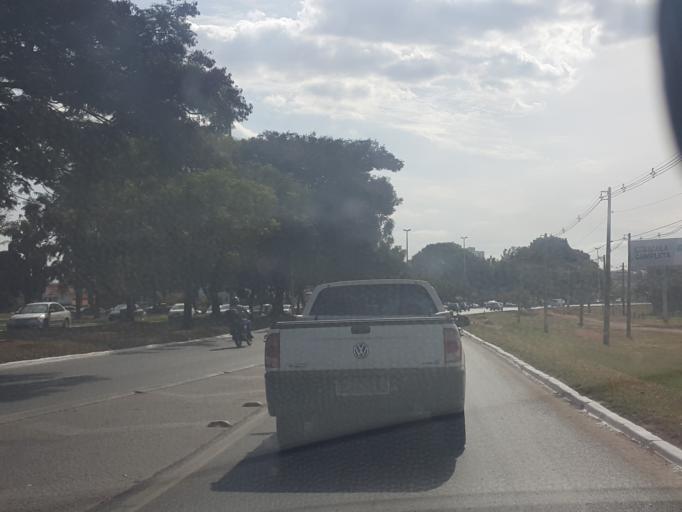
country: BR
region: Federal District
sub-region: Brasilia
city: Brasilia
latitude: -15.8299
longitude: -48.0513
